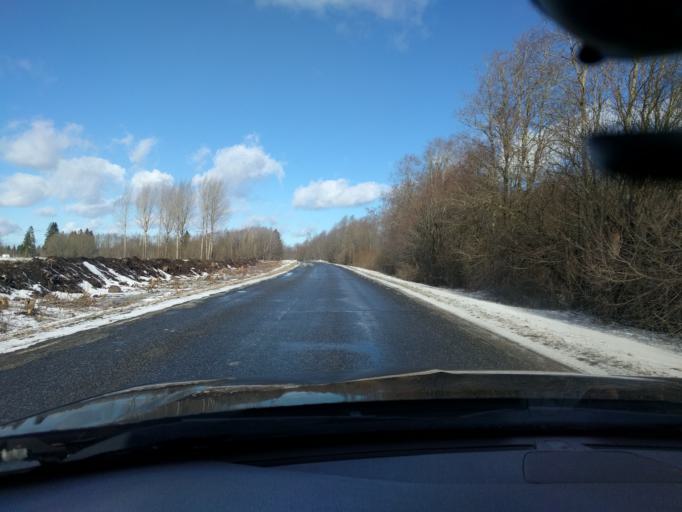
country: EE
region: Harju
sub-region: Raasiku vald
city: Raasiku
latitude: 59.3029
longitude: 25.1715
